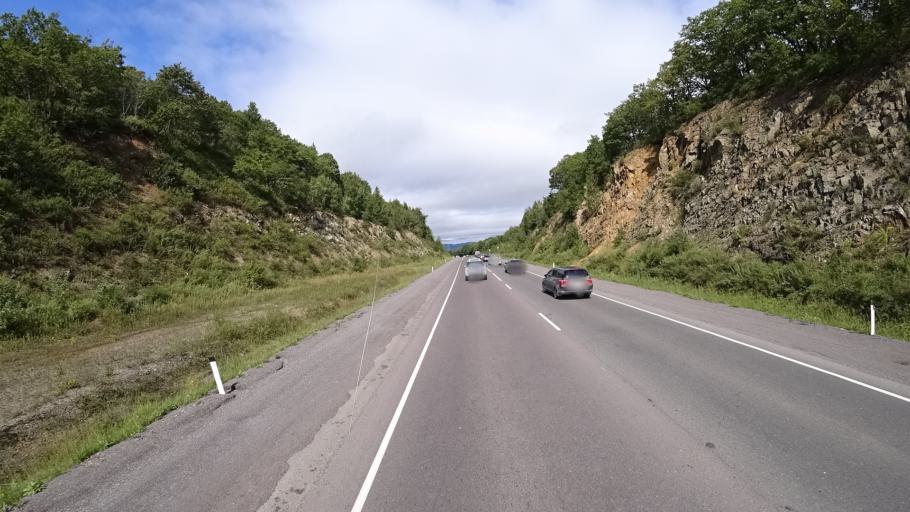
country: RU
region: Primorskiy
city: Lyalichi
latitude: 44.1279
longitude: 132.4254
